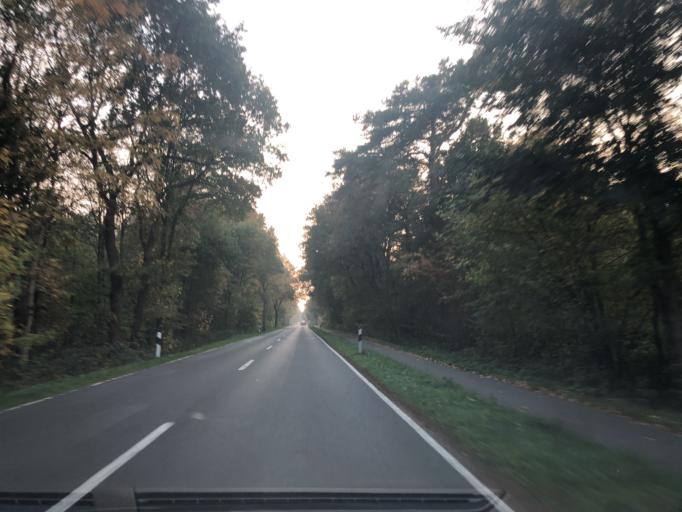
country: DE
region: Lower Saxony
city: Wardenburg
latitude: 53.0460
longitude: 8.1273
